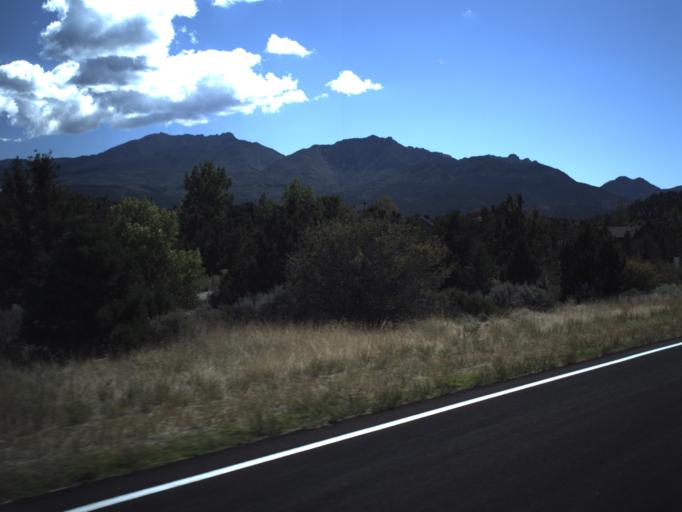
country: US
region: Utah
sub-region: Washington County
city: Enterprise
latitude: 37.4280
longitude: -113.6293
